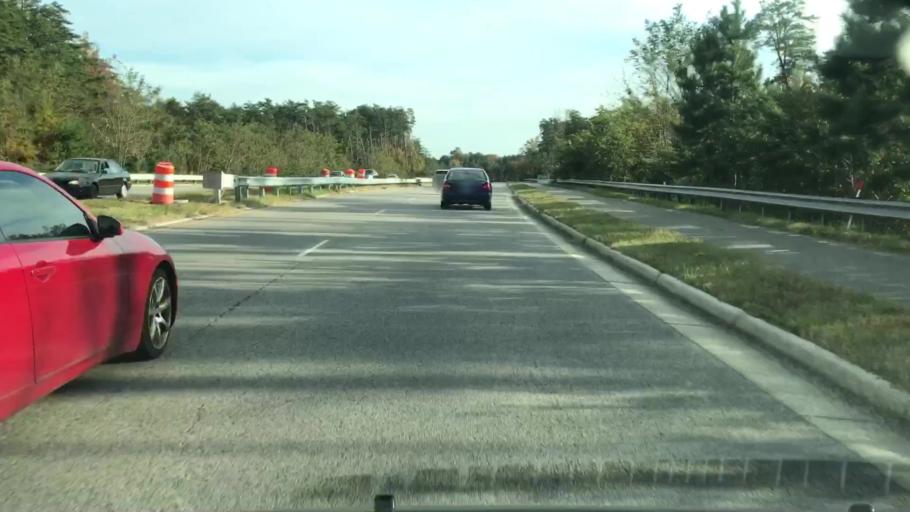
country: US
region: Virginia
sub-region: Fairfax County
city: Woodlawn
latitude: 38.7321
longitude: -77.1437
